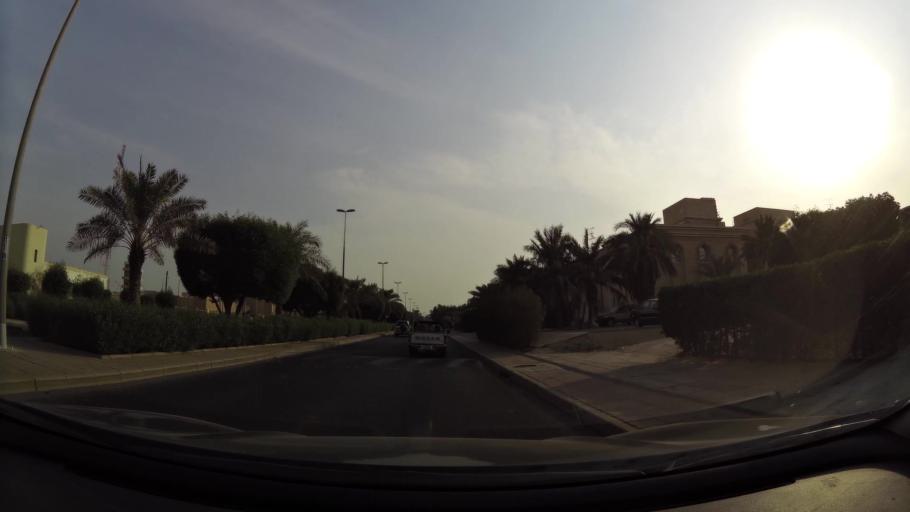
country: KW
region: Mubarak al Kabir
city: Mubarak al Kabir
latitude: 29.2023
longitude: 48.0689
